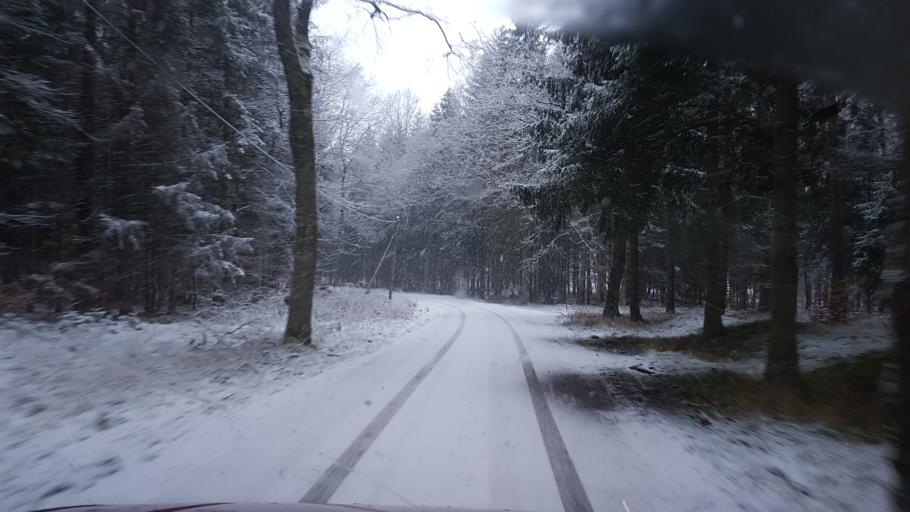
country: PL
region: West Pomeranian Voivodeship
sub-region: Powiat slawienski
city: Slawno
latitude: 54.2473
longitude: 16.6875
